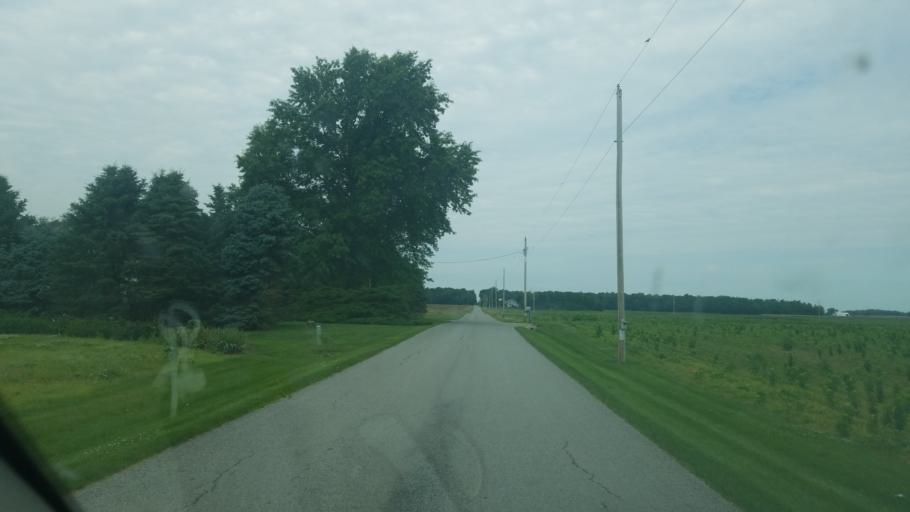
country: US
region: Ohio
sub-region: Seneca County
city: Fostoria
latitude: 41.0502
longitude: -83.4446
